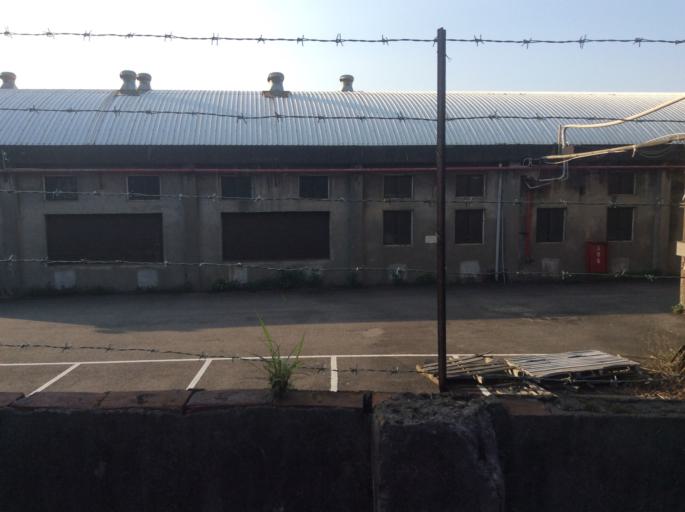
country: TW
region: Taiwan
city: Taoyuan City
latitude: 24.9718
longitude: 121.2025
